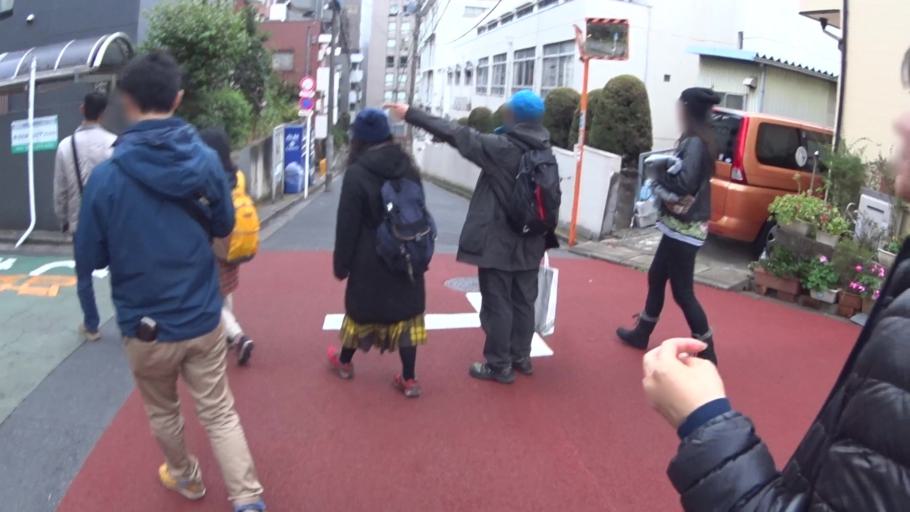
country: JP
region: Tokyo
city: Tokyo
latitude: 35.6920
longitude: 139.7170
